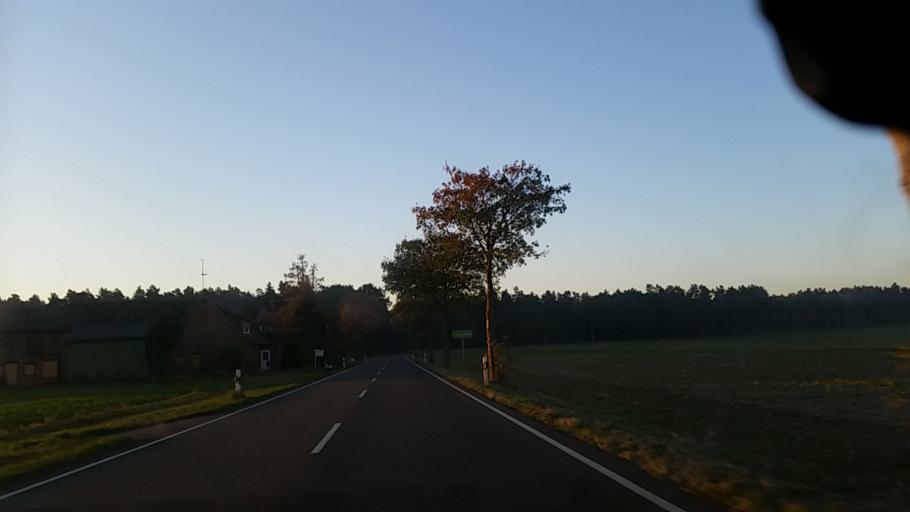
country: DE
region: Lower Saxony
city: Luder
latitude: 52.7890
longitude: 10.7155
